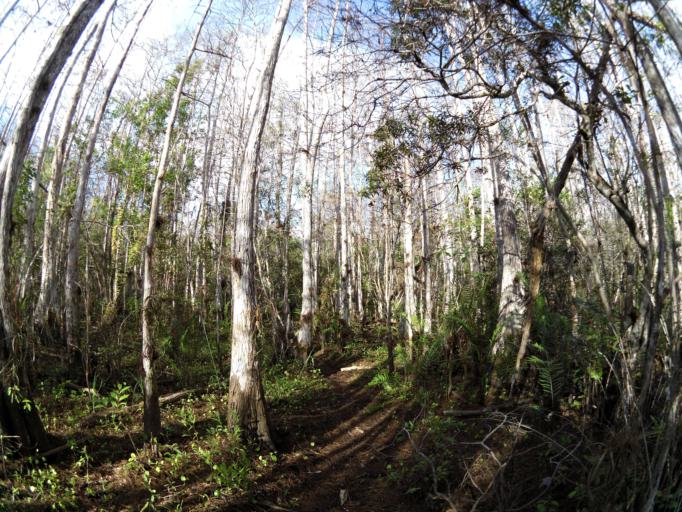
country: US
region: Florida
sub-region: Collier County
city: Lely Resort
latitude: 26.0039
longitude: -81.5934
